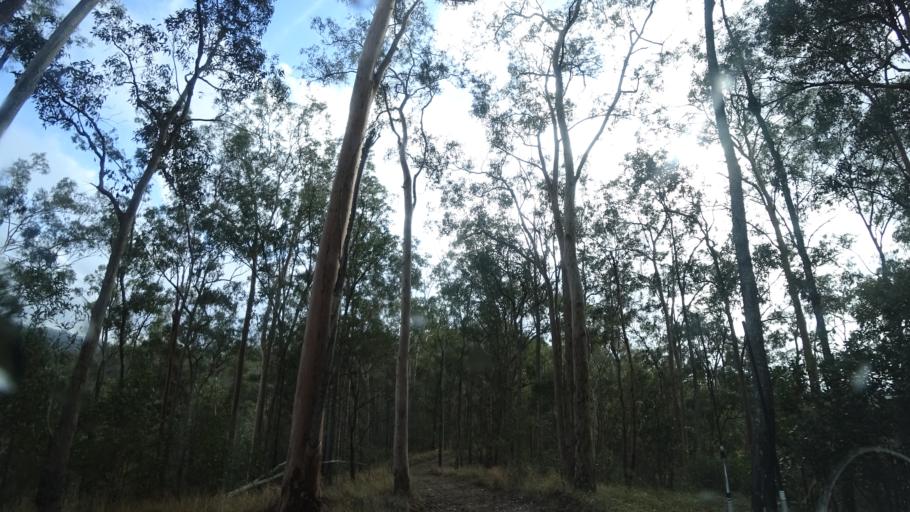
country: AU
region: Queensland
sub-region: Brisbane
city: Pullenvale
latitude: -27.4630
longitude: 152.8648
